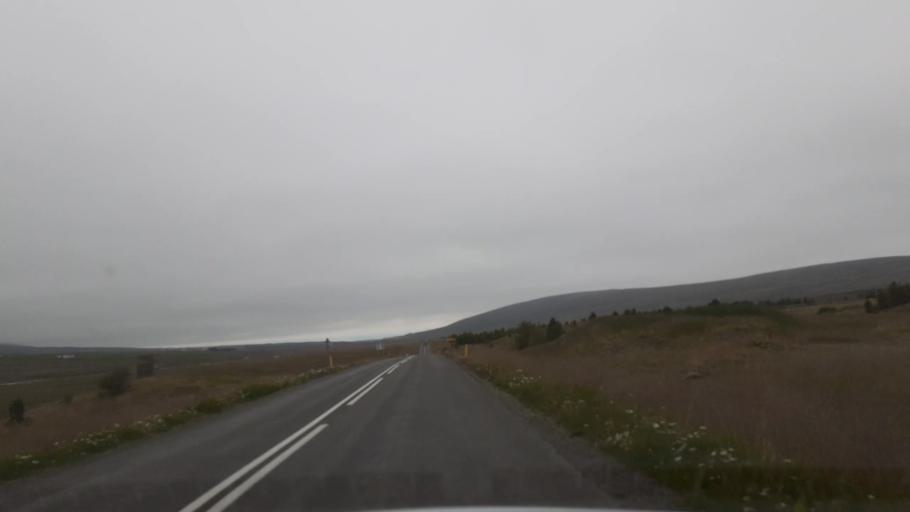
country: IS
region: Northeast
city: Siglufjoerdur
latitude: 65.7367
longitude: -19.1270
